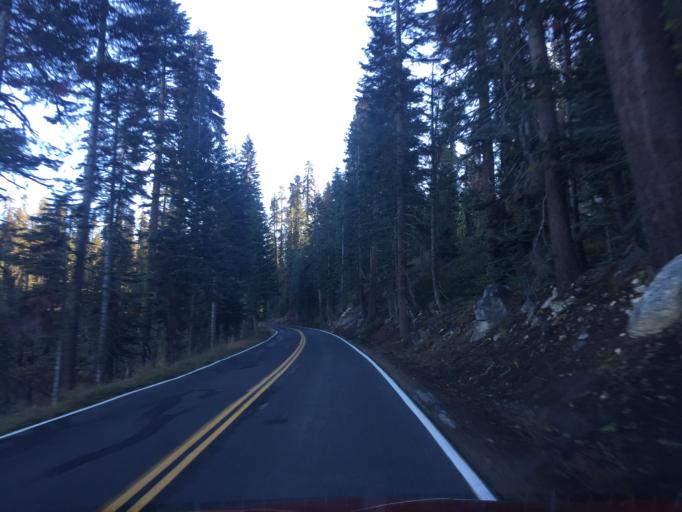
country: US
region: California
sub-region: Mariposa County
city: Yosemite Valley
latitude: 37.6691
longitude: -119.6594
